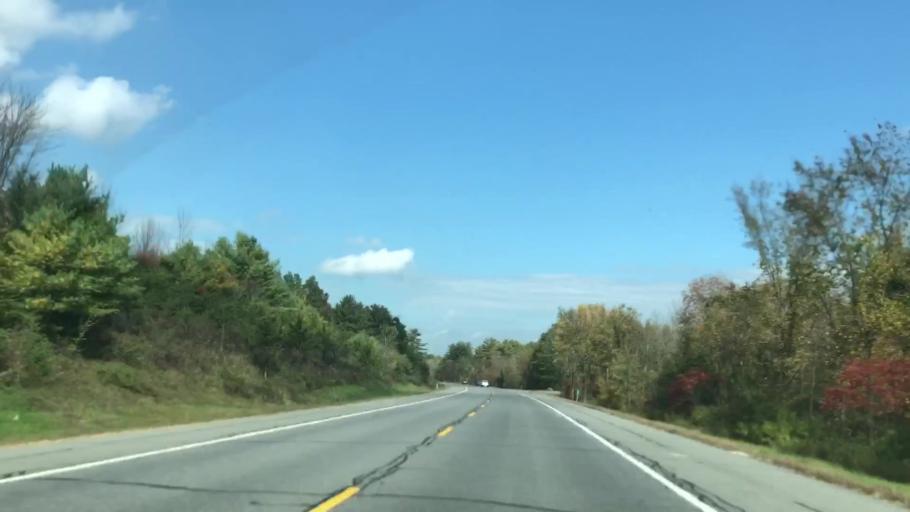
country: US
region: New York
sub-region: Washington County
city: Whitehall
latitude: 43.4445
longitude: -73.4526
